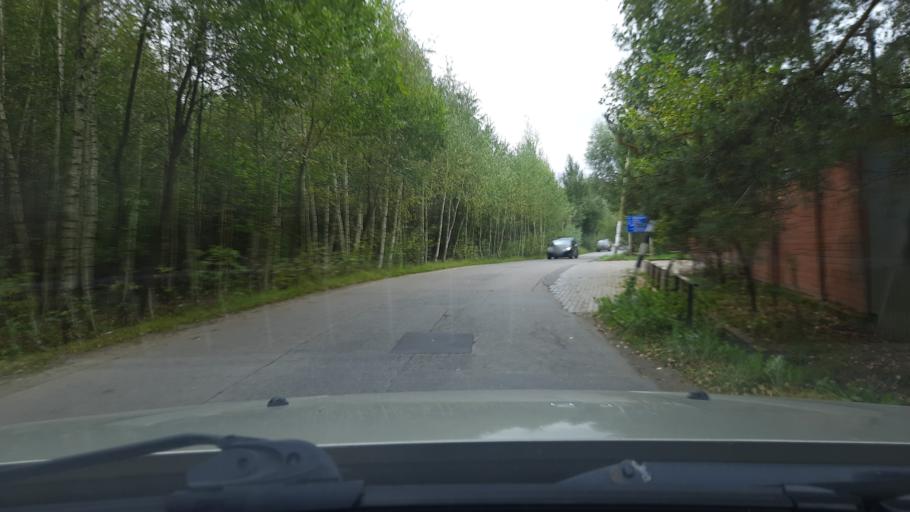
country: RU
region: Moskovskaya
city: Barvikha
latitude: 55.7259
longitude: 37.3017
